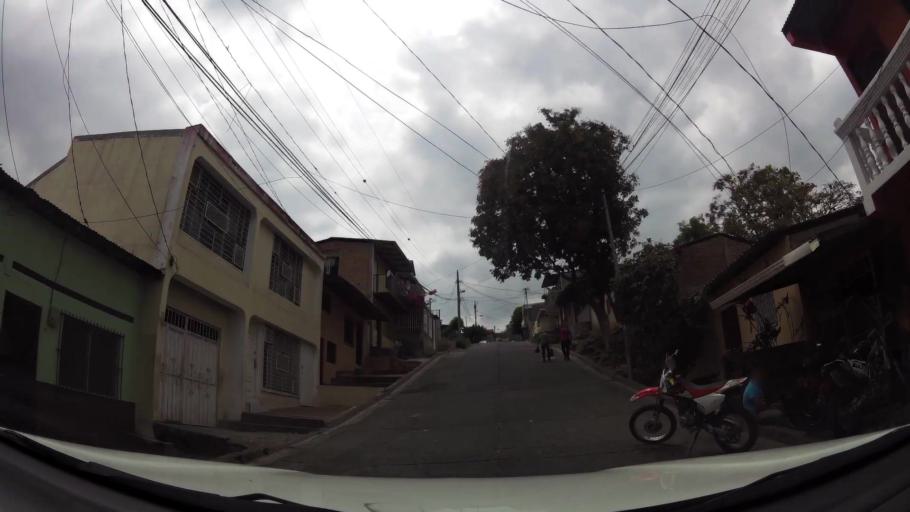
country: NI
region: Matagalpa
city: Matagalpa
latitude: 12.9249
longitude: -85.9149
